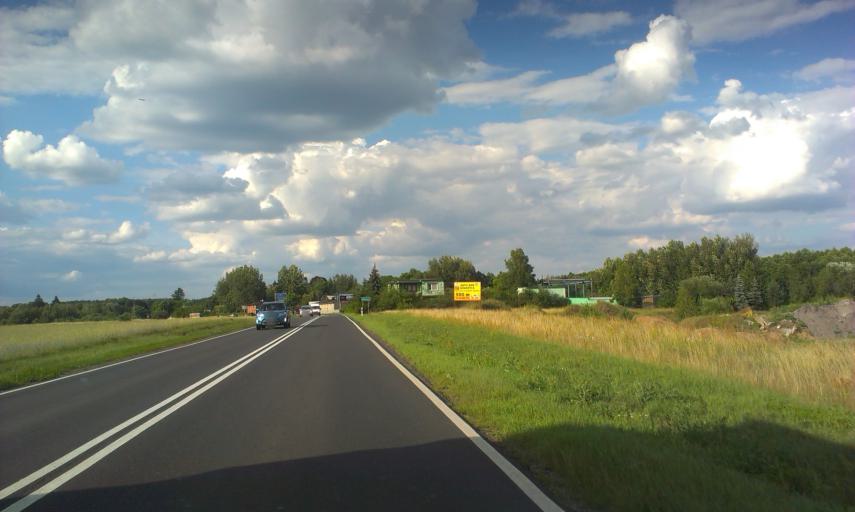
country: PL
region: Greater Poland Voivodeship
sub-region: Powiat pilski
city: Pila
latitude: 53.2134
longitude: 16.7847
